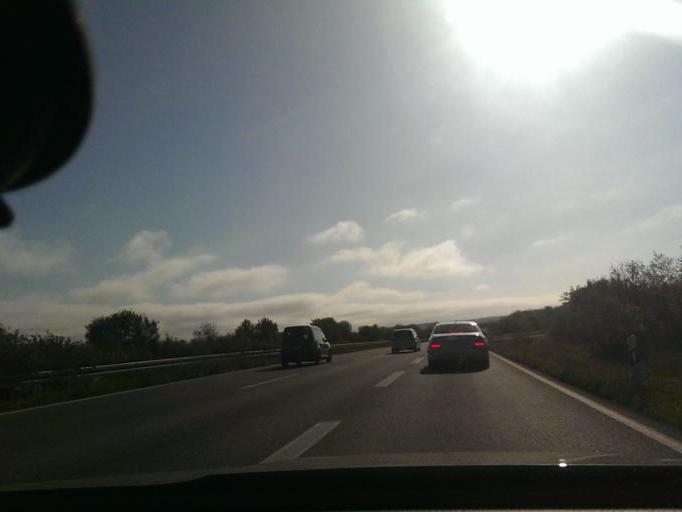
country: DE
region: Saxony-Anhalt
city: Stapelburg
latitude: 51.9355
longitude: 10.6327
